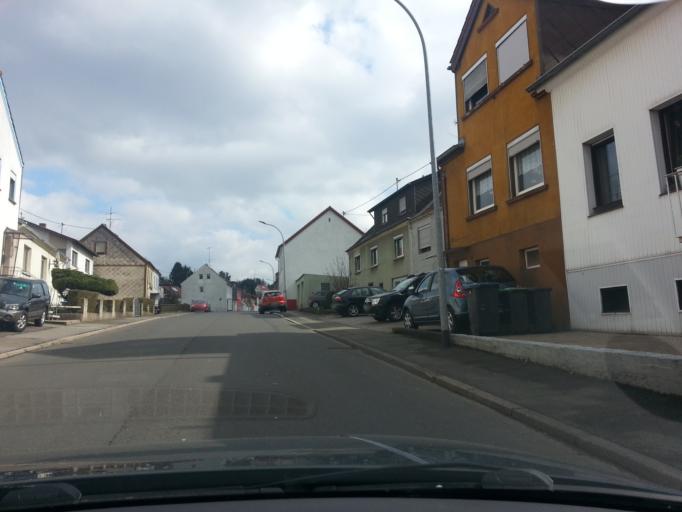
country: DE
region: Saarland
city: Hangard
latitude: 49.3702
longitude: 7.1947
